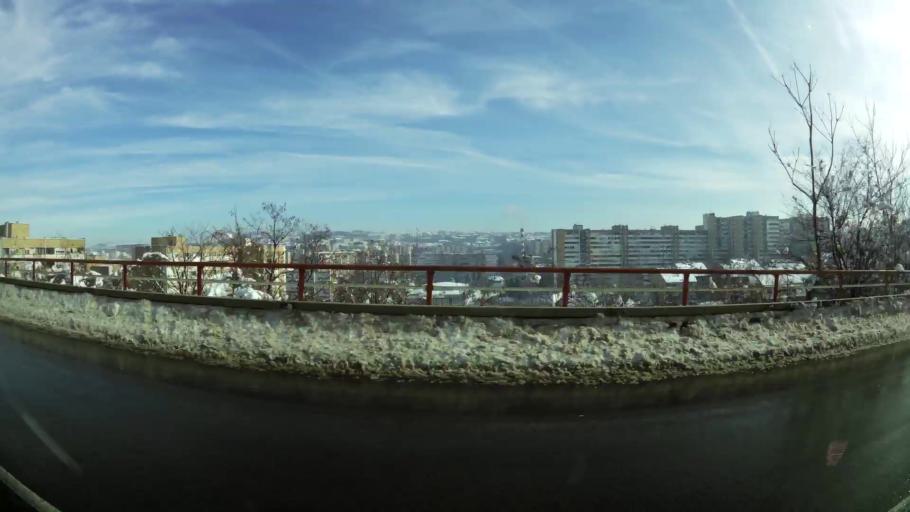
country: RS
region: Central Serbia
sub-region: Belgrade
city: Zvezdara
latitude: 44.7893
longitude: 20.5266
